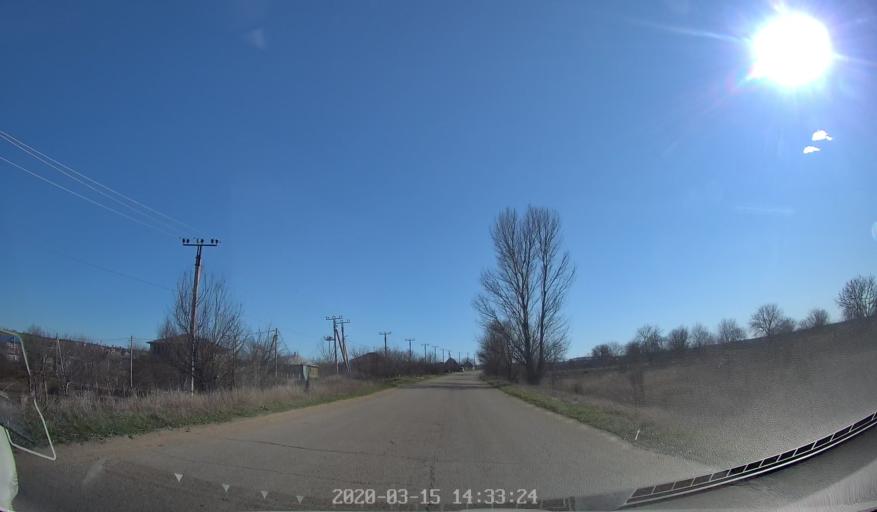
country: MD
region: Orhei
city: Orhei
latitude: 47.3378
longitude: 28.9170
